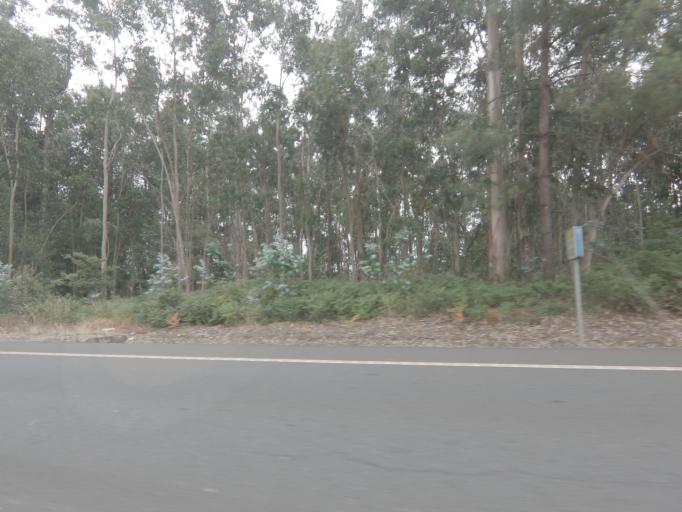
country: ES
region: Galicia
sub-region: Provincia de Pontevedra
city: Tomino
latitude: 41.9825
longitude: -8.7223
